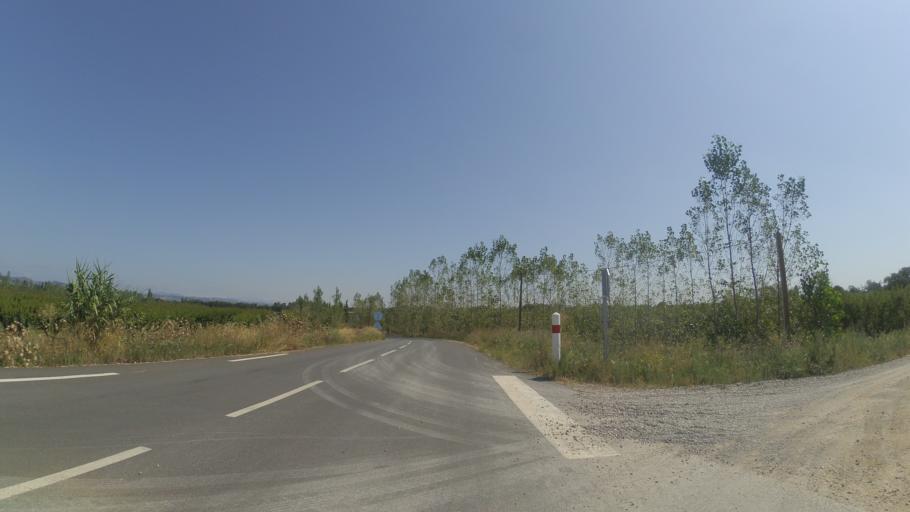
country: FR
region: Languedoc-Roussillon
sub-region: Departement des Pyrenees-Orientales
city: Corneilla-la-Riviere
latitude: 42.6574
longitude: 2.7184
